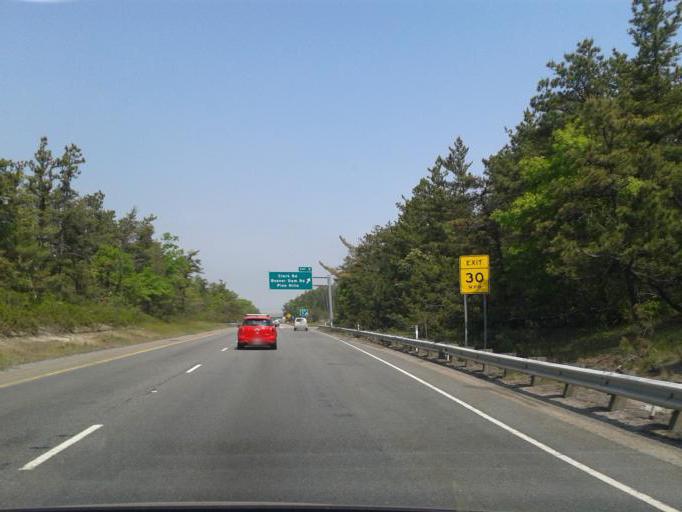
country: US
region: Massachusetts
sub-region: Plymouth County
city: White Island Shores
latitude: 41.8705
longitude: -70.5978
